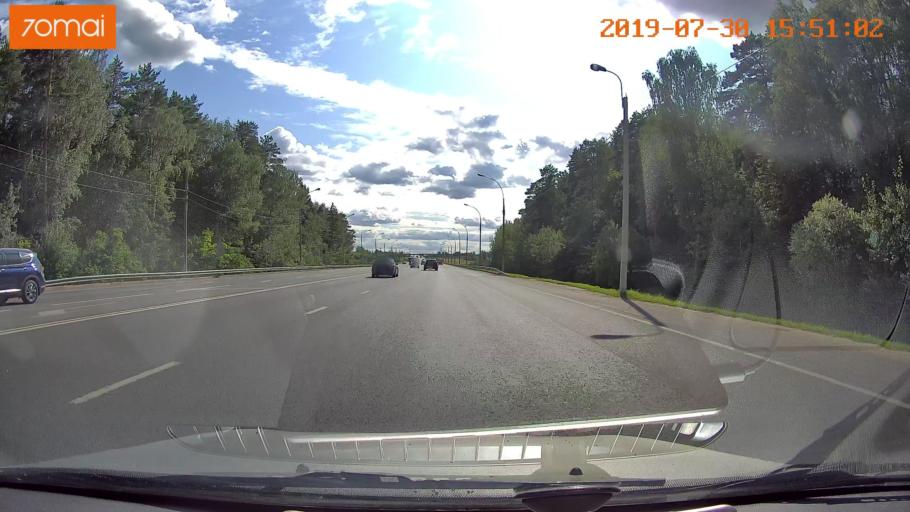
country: RU
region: Moskovskaya
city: Voskresensk
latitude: 55.3292
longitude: 38.6468
